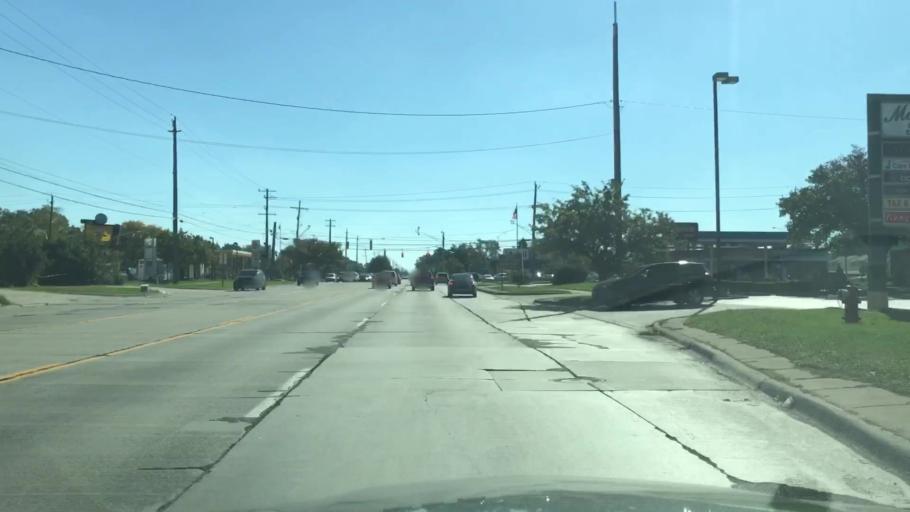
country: US
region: Michigan
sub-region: Oakland County
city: Madison Heights
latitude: 42.5215
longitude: -83.0862
